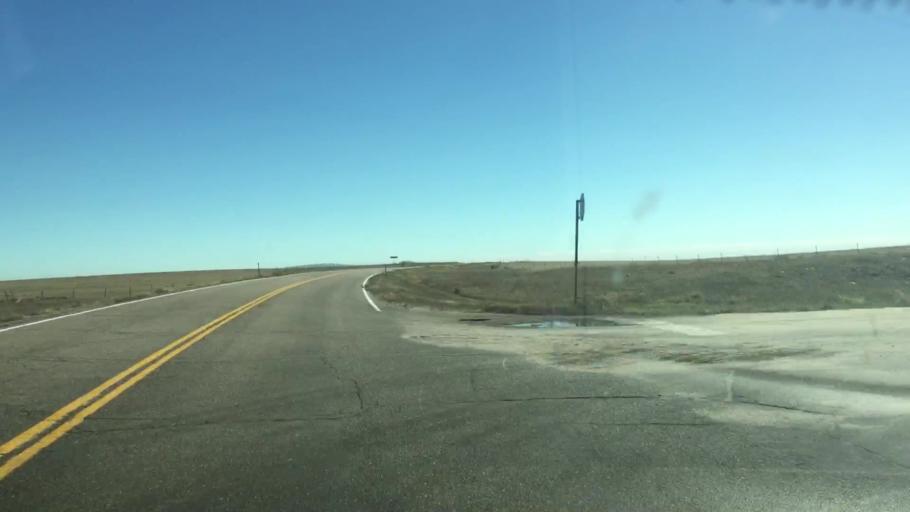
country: US
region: Colorado
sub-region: Lincoln County
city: Limon
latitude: 39.2877
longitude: -103.9750
